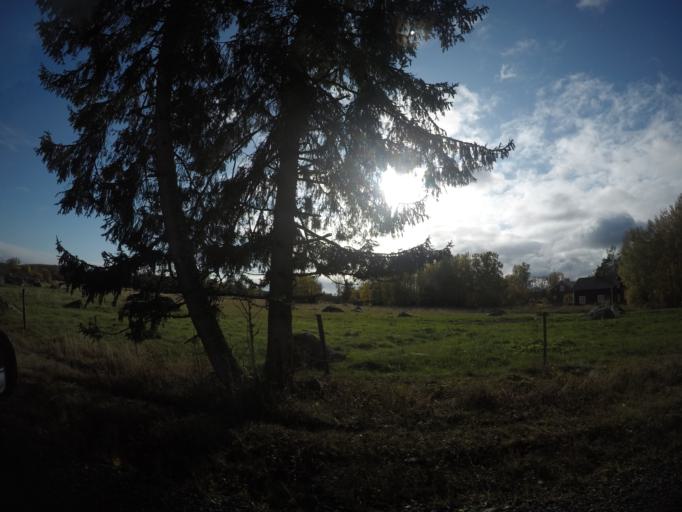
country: SE
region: Soedermanland
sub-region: Eskilstuna Kommun
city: Kvicksund
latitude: 59.3810
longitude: 16.2516
